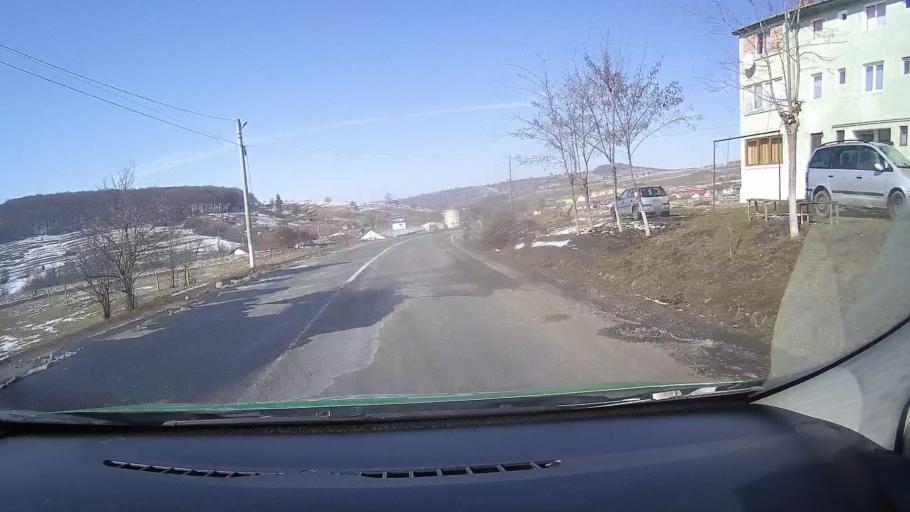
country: RO
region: Brasov
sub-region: Oras Rupea
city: Rupea
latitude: 46.0352
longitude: 25.2054
